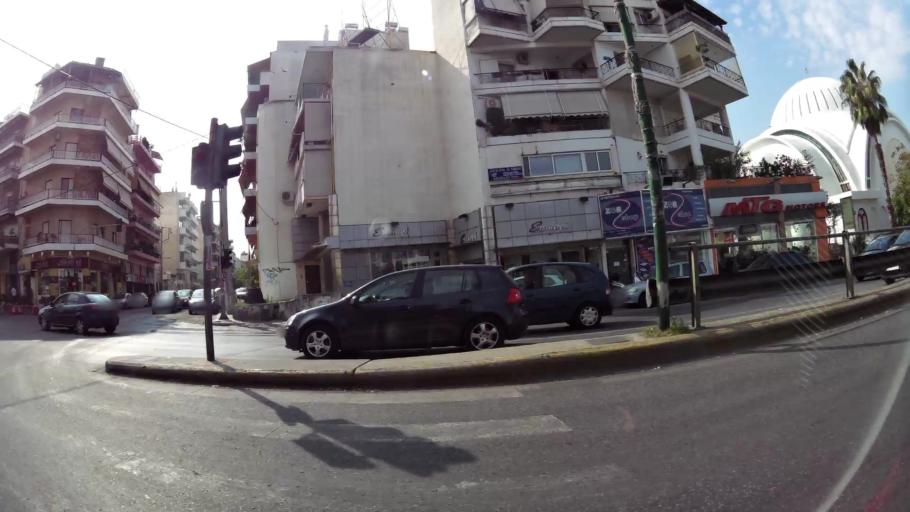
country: GR
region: Attica
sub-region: Nomarchia Athinas
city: Dhafni
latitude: 37.9565
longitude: 23.7241
